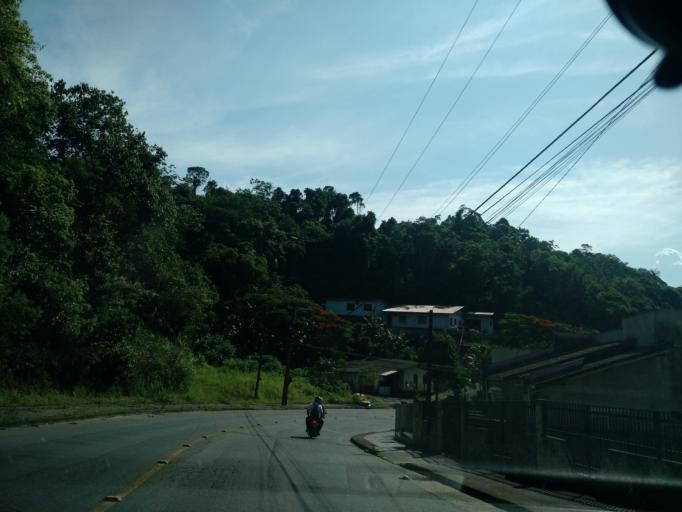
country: BR
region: Santa Catarina
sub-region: Jaragua Do Sul
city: Jaragua do Sul
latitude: -26.4964
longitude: -49.1008
